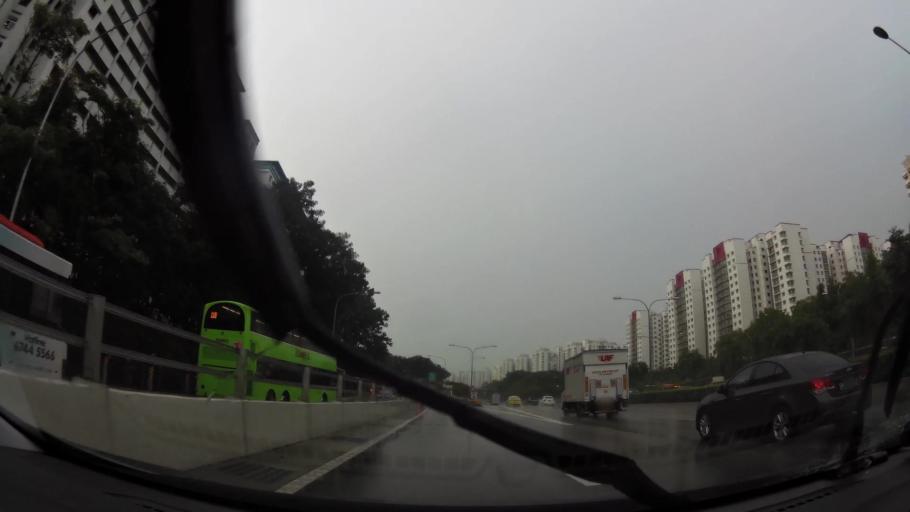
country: MY
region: Johor
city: Kampung Pasir Gudang Baru
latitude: 1.3951
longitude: 103.9058
